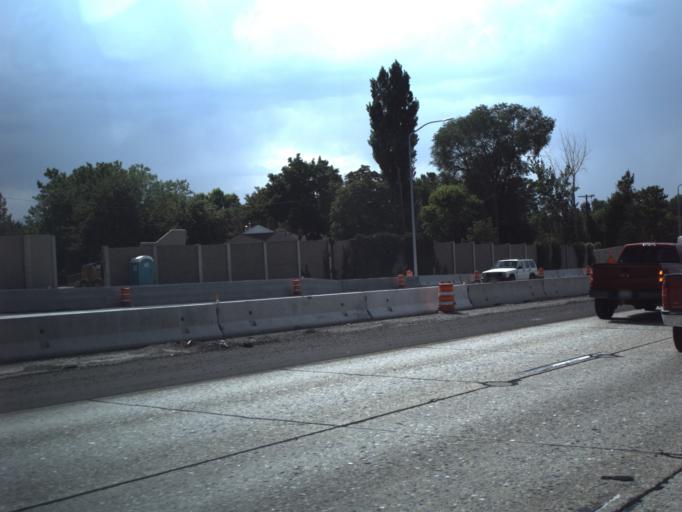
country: US
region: Utah
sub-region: Salt Lake County
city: Canyon Rim
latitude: 40.7146
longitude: -111.8279
